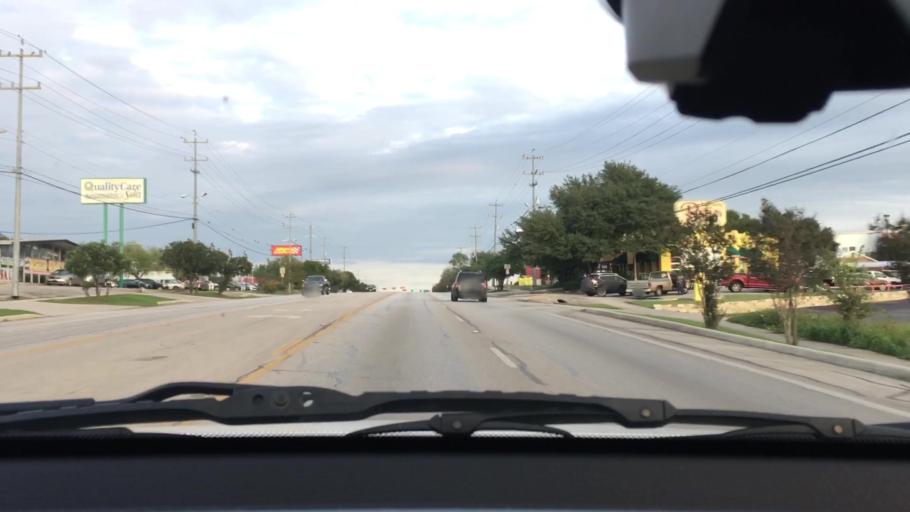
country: US
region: Texas
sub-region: Bexar County
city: Universal City
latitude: 29.5517
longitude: -98.3026
